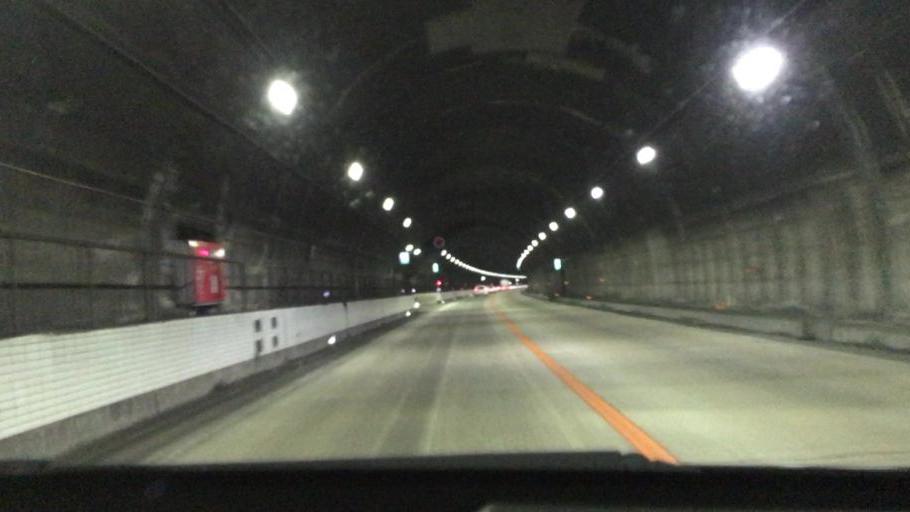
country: JP
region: Yamaguchi
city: Tokuyama
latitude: 34.0852
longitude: 131.7448
